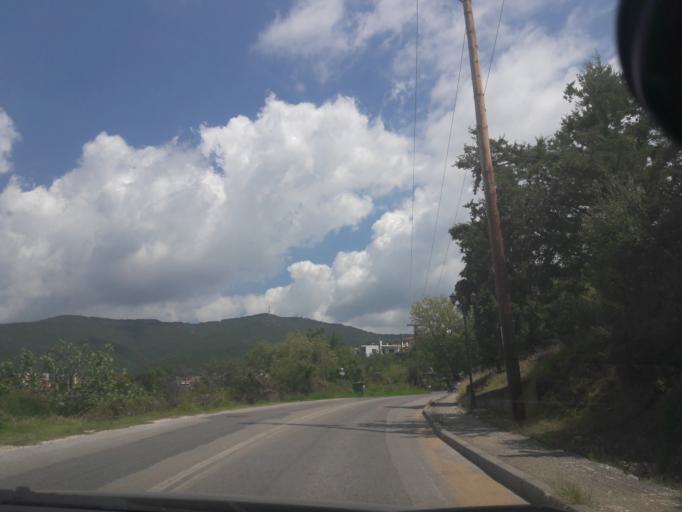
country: GR
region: Central Macedonia
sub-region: Nomos Chalkidikis
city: Polygyros
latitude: 40.3737
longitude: 23.4351
